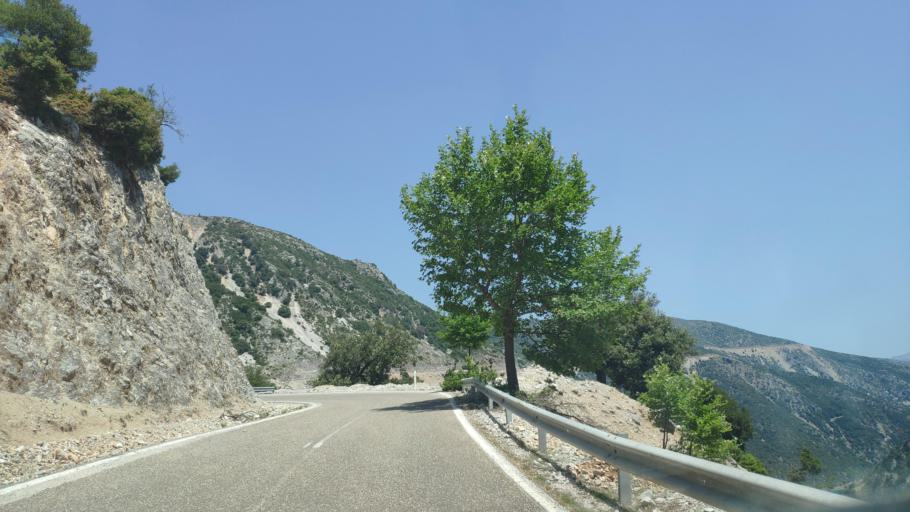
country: GR
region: West Greece
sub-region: Nomos Aitolias kai Akarnanias
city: Krikellos
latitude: 39.0139
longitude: 21.3723
